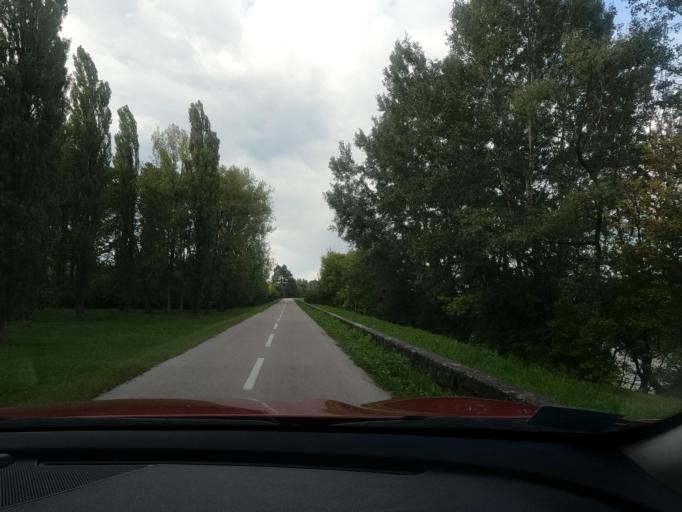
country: HR
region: Sisacko-Moslavacka
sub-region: Grad Sisak
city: Sisak
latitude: 45.4739
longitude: 16.3847
